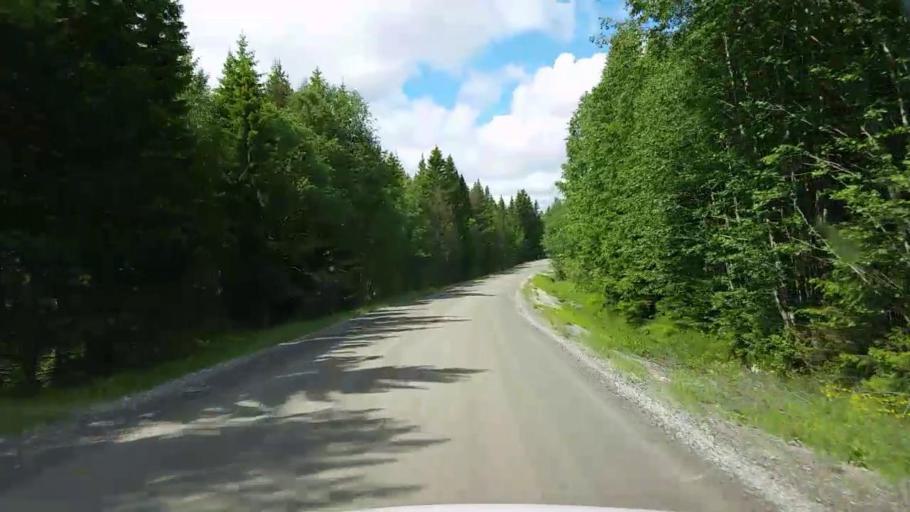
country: SE
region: Gaevleborg
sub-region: Bollnas Kommun
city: Vittsjo
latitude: 61.0459
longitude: 16.3372
